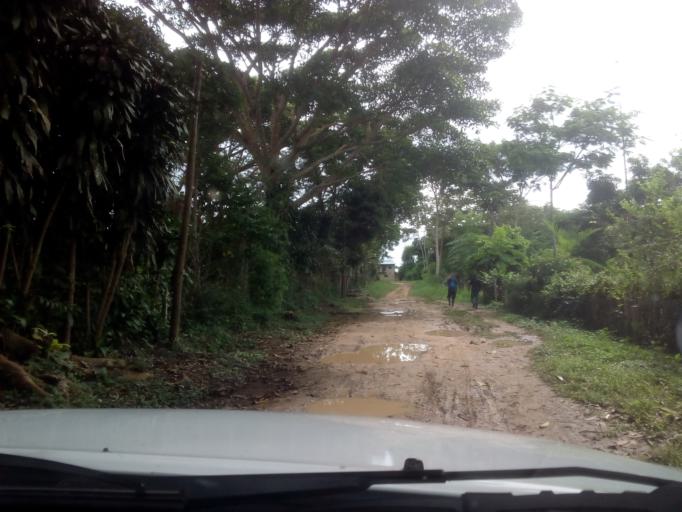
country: PE
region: San Martin
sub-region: Provincia de Lamas
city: Lamas
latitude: -6.4108
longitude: -76.4664
